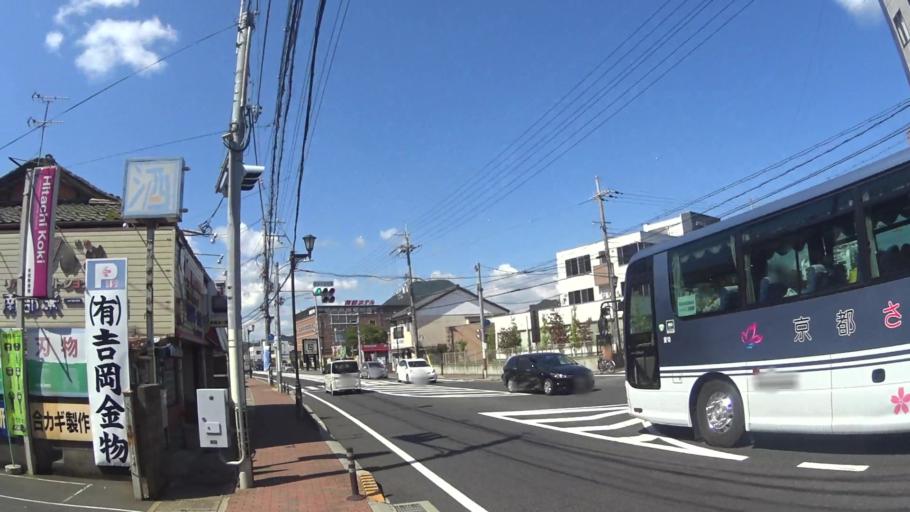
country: JP
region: Kyoto
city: Maizuru
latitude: 35.4511
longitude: 135.3235
